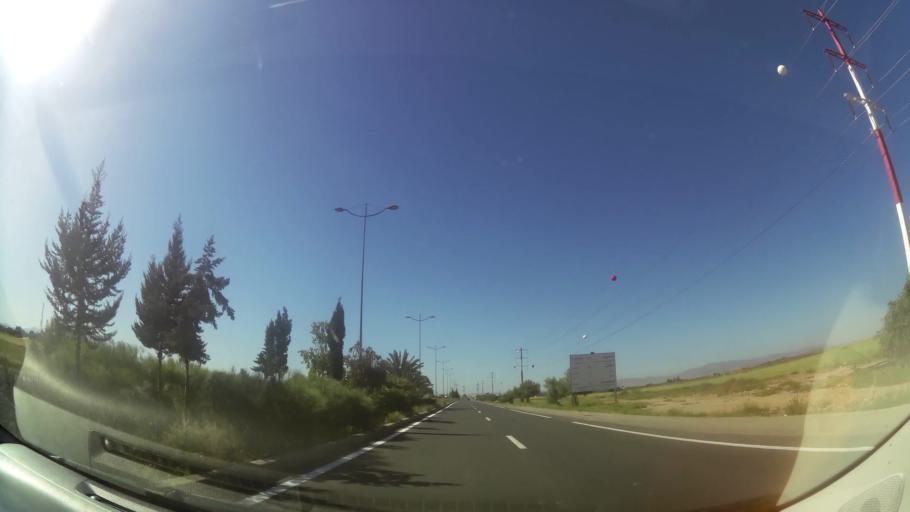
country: MA
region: Oriental
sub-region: Oujda-Angad
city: Oujda
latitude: 34.7403
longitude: -1.9299
